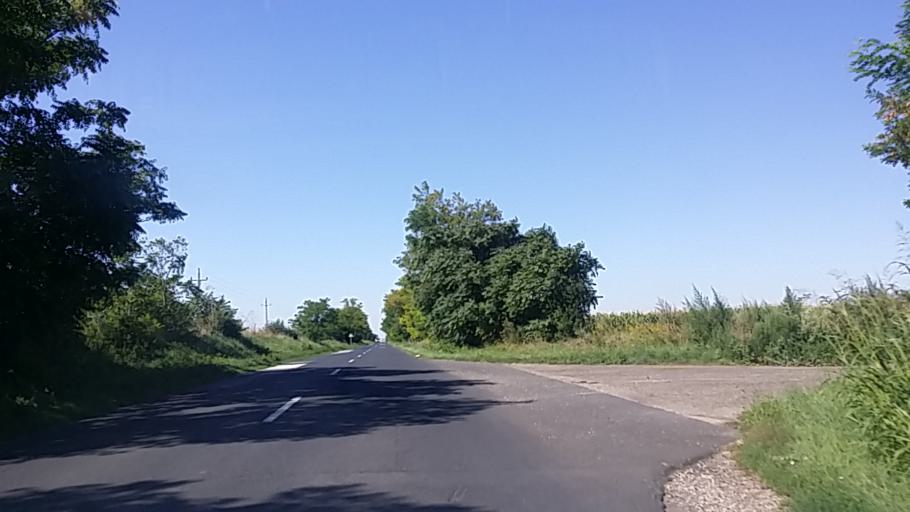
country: HU
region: Fejer
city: Sarbogard
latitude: 46.8860
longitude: 18.6915
